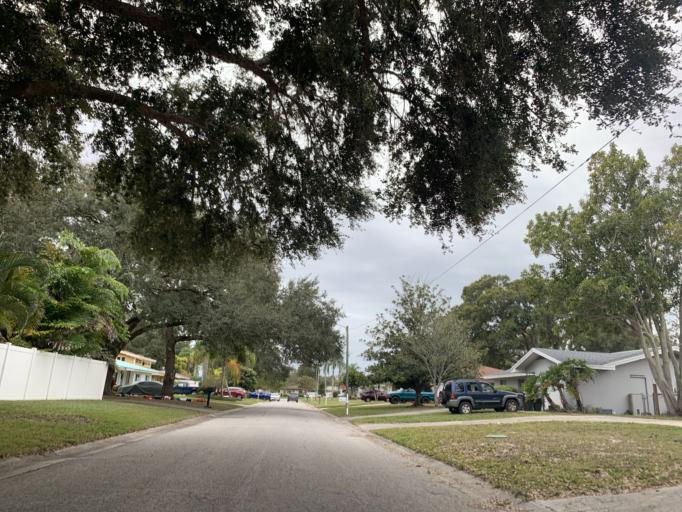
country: US
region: Florida
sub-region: Pinellas County
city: Belleair
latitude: 27.9370
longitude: -82.7813
